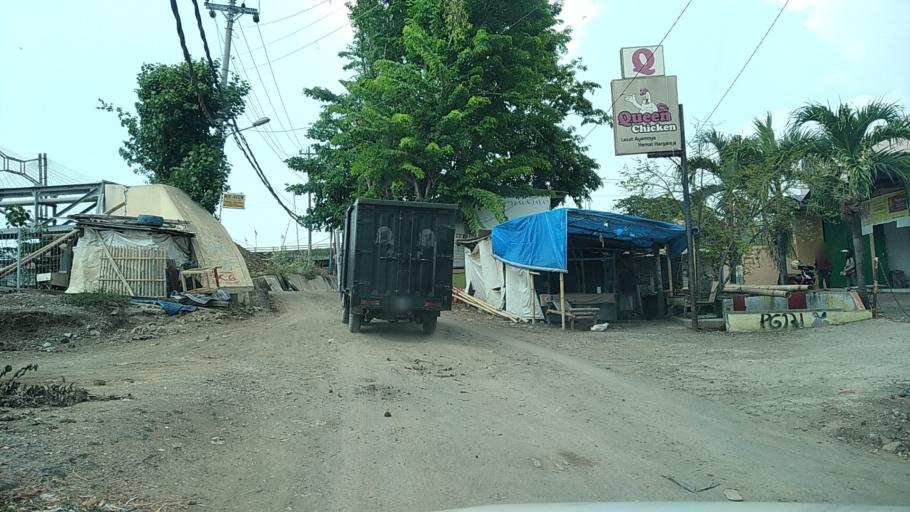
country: ID
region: Central Java
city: Semarang
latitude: -6.9867
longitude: 110.4414
